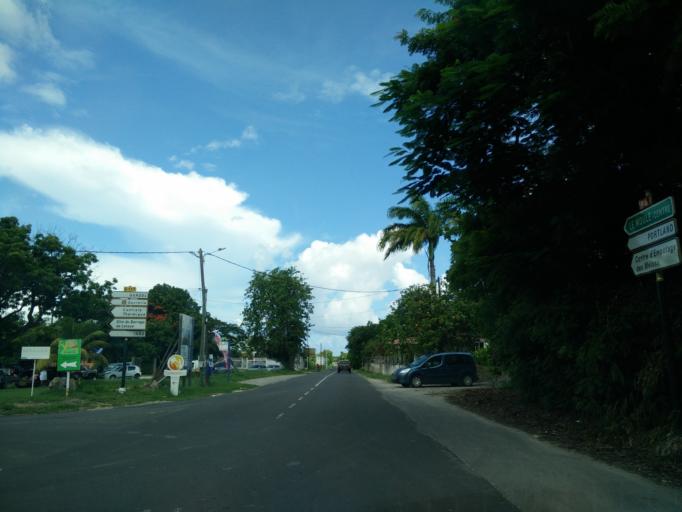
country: GP
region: Guadeloupe
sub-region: Guadeloupe
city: Le Moule
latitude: 16.3107
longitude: -61.3158
